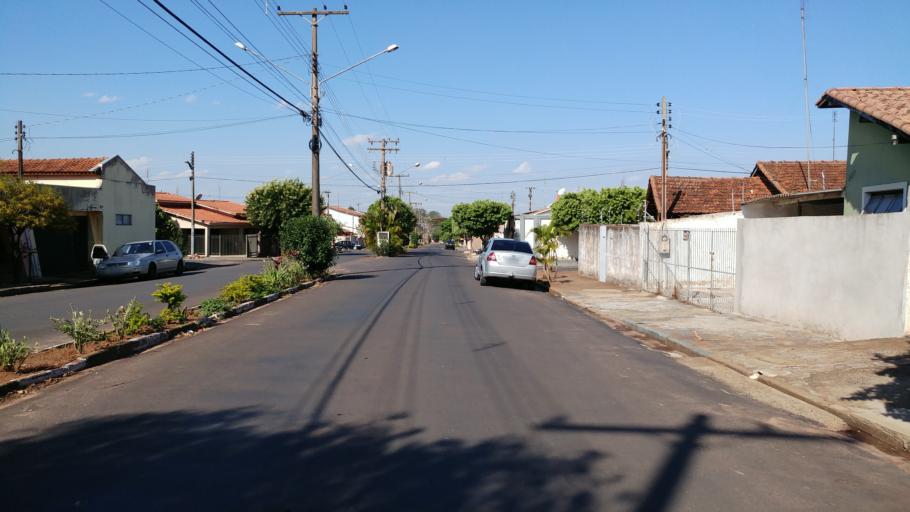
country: BR
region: Sao Paulo
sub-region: Paraguacu Paulista
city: Paraguacu Paulista
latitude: -22.4271
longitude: -50.5754
